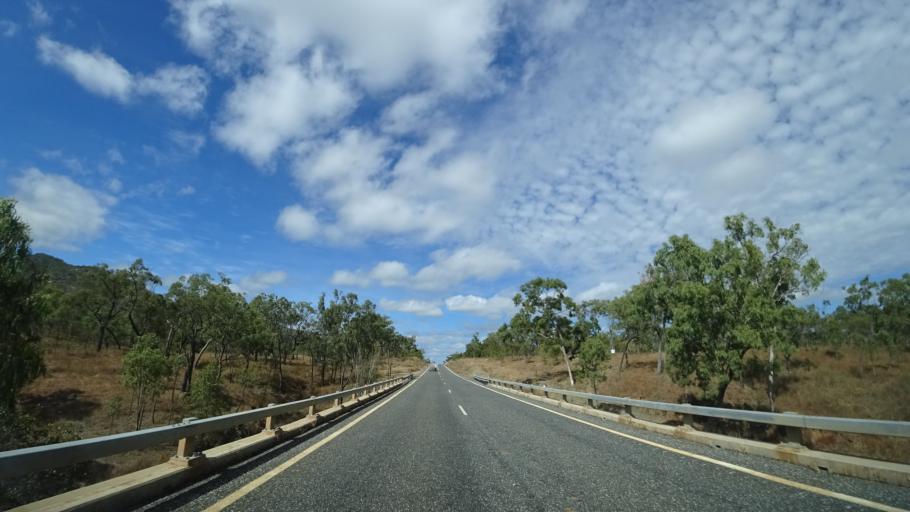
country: AU
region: Queensland
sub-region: Cairns
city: Port Douglas
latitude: -16.3251
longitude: 144.7202
